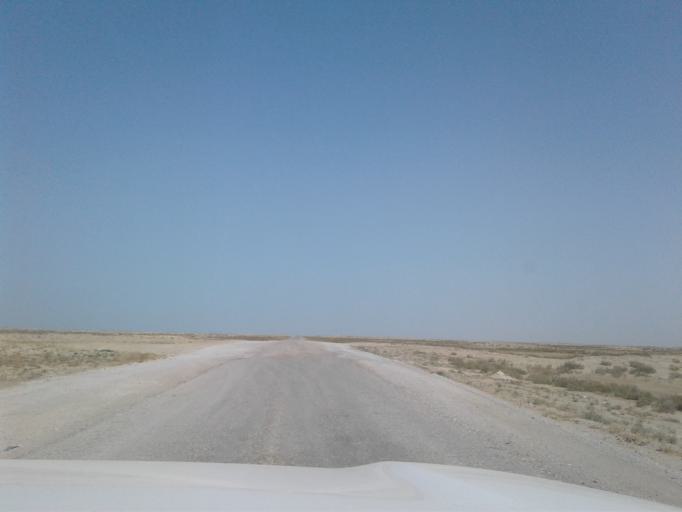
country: IR
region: Golestan
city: Gomishan
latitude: 37.9181
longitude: 53.8488
